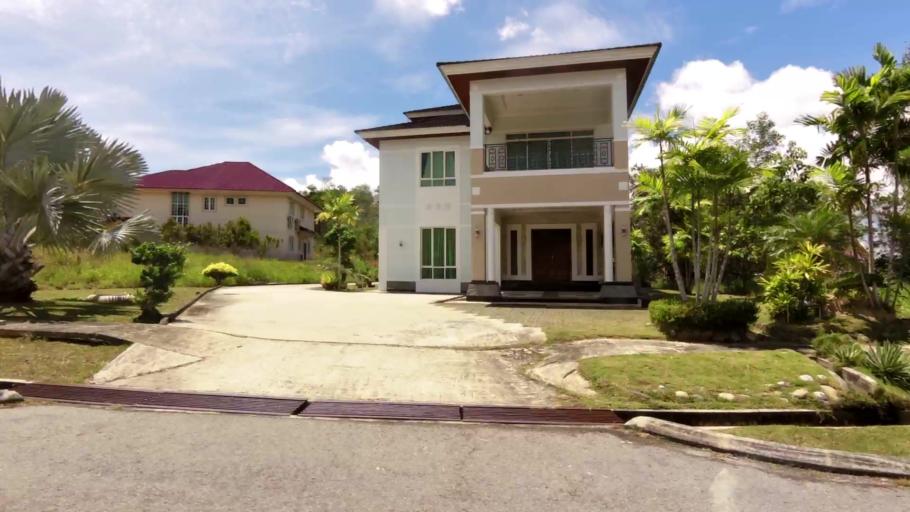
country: BN
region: Brunei and Muara
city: Bandar Seri Begawan
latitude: 4.9720
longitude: 114.9086
